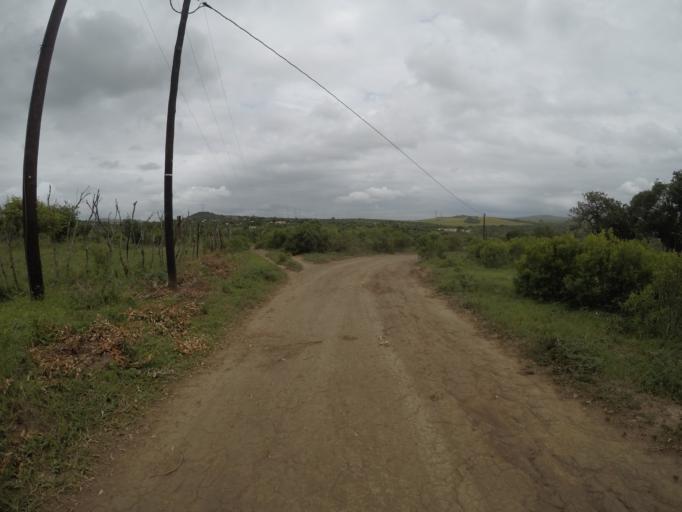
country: ZA
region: KwaZulu-Natal
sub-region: uThungulu District Municipality
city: Empangeni
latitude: -28.5983
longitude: 31.8309
